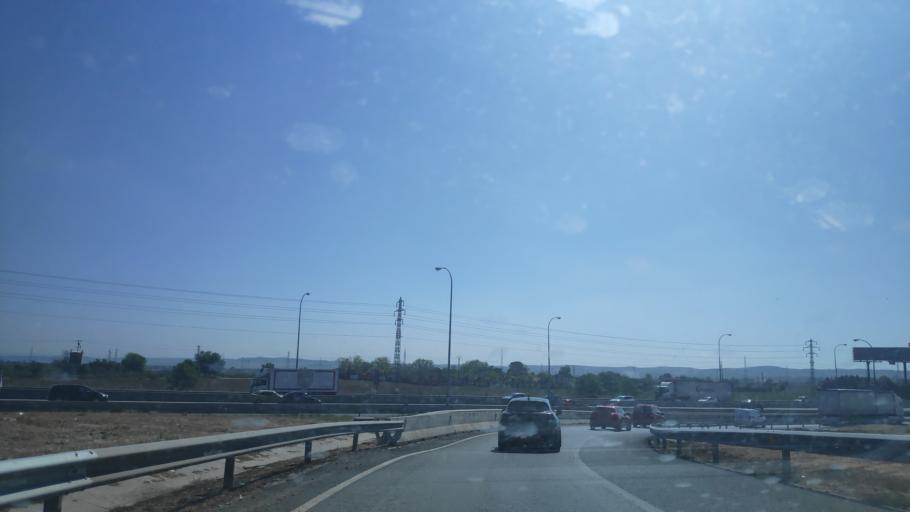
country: ES
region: Madrid
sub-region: Provincia de Madrid
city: Getafe
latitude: 40.3025
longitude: -3.6926
